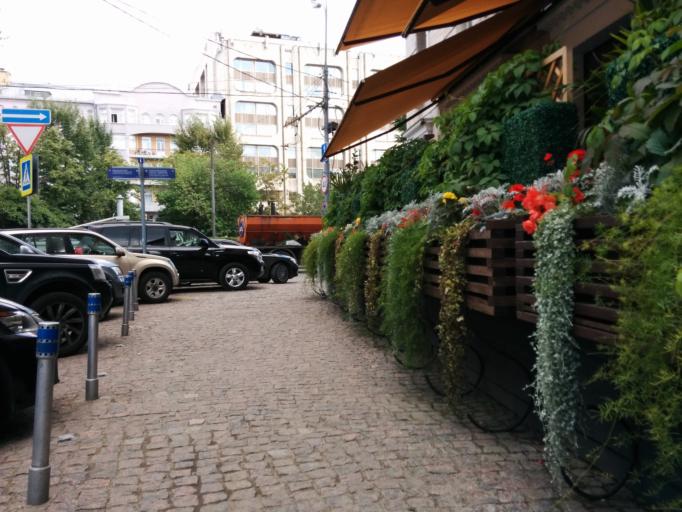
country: RU
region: Moscow
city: Moscow
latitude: 55.7588
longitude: 37.5982
